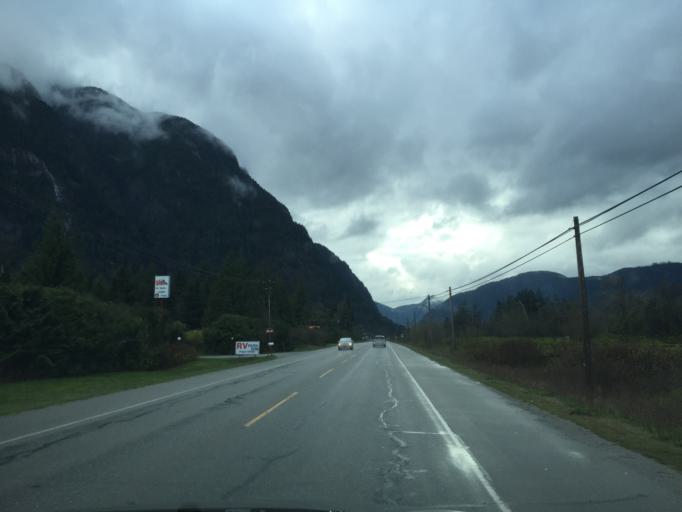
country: CA
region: British Columbia
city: Hope
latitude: 49.3669
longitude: -121.5058
